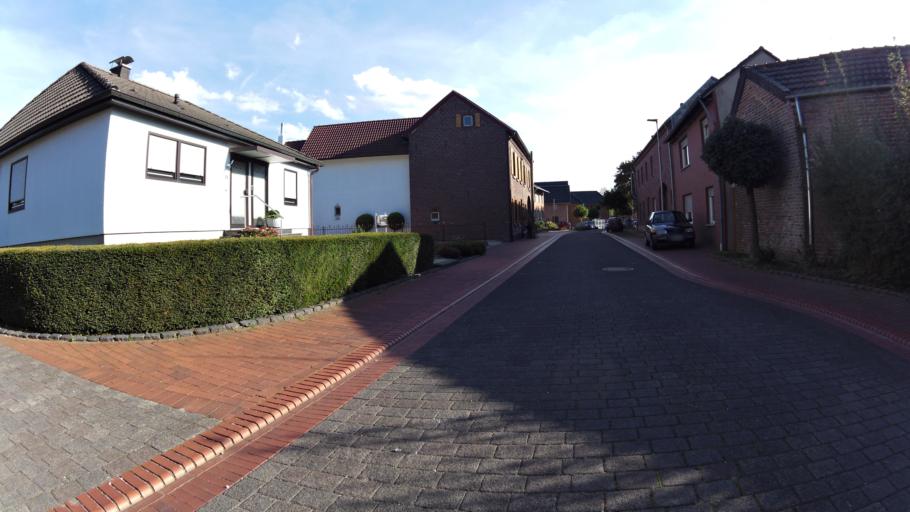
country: DE
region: North Rhine-Westphalia
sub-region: Regierungsbezirk Koln
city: Ubach-Palenberg
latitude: 50.9418
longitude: 6.0548
